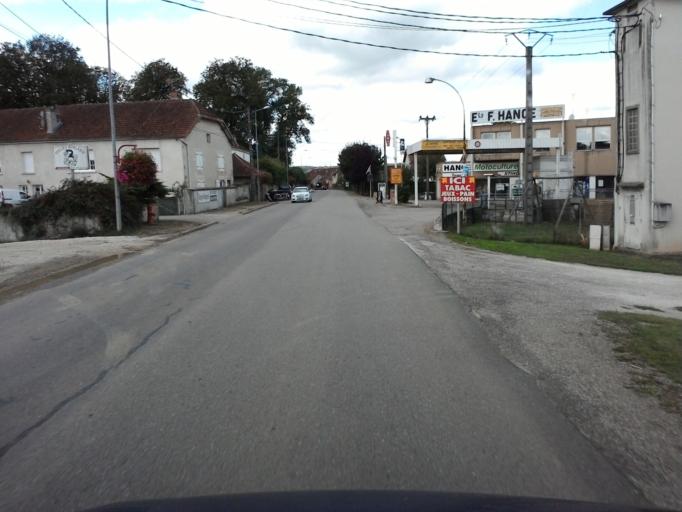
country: FR
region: Lorraine
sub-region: Departement des Vosges
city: Liffol-le-Grand
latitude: 48.3177
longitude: 5.5907
